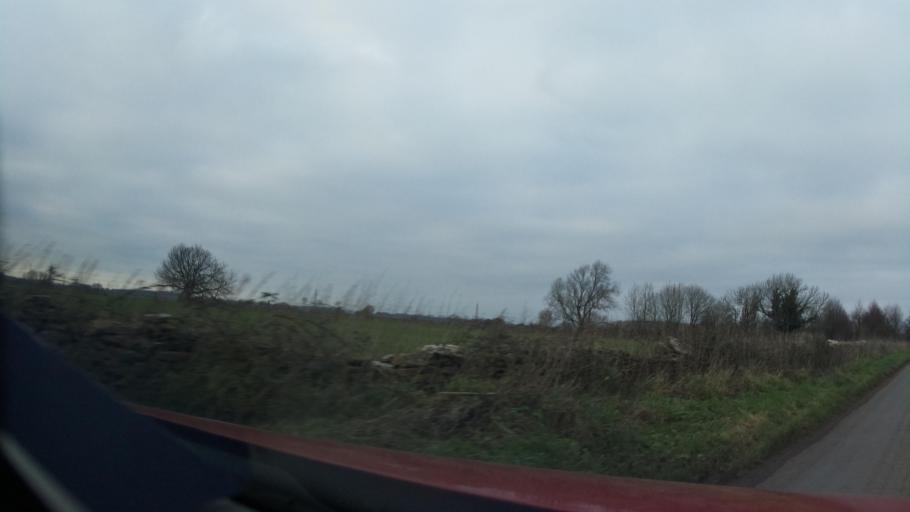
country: GB
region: England
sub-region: Wiltshire
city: Nettleton
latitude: 51.4892
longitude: -2.2795
